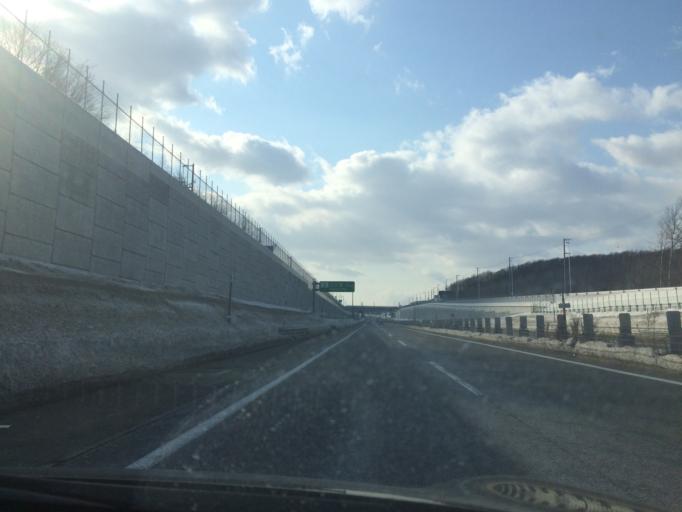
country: JP
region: Hokkaido
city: Kitahiroshima
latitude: 42.9988
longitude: 141.4683
